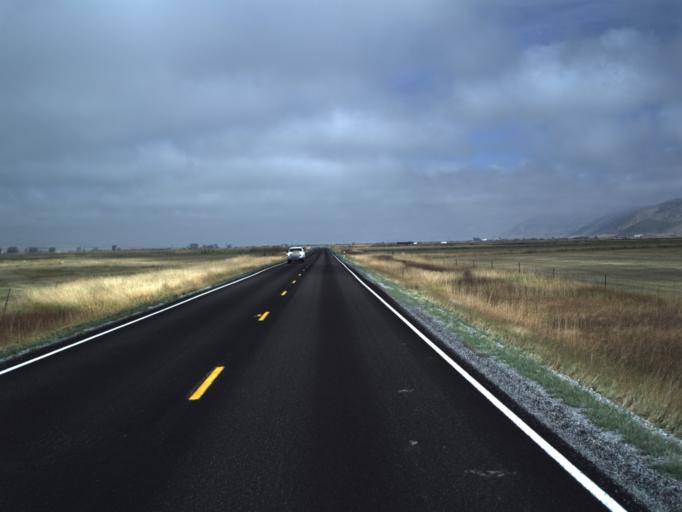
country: US
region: Utah
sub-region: Rich County
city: Randolph
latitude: 41.4957
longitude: -111.1211
